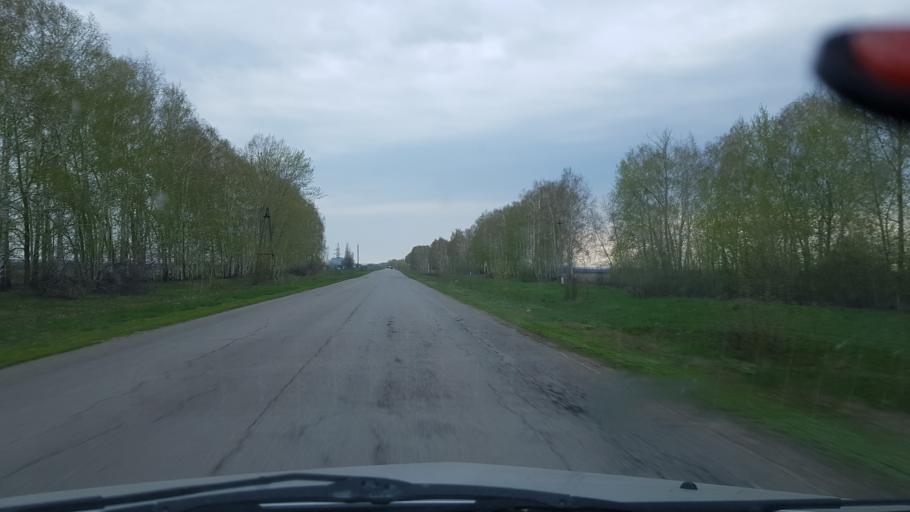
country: RU
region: Samara
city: Podstepki
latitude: 53.6655
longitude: 49.1694
